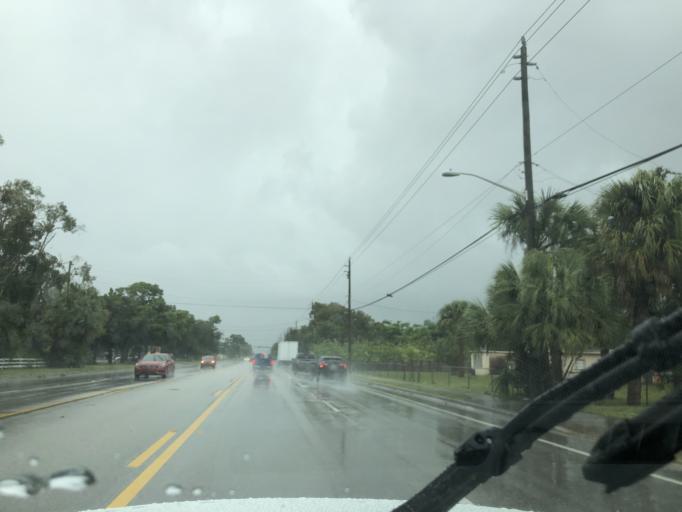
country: US
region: Florida
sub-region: Palm Beach County
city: Haverhill
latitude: 26.6953
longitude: -80.1197
